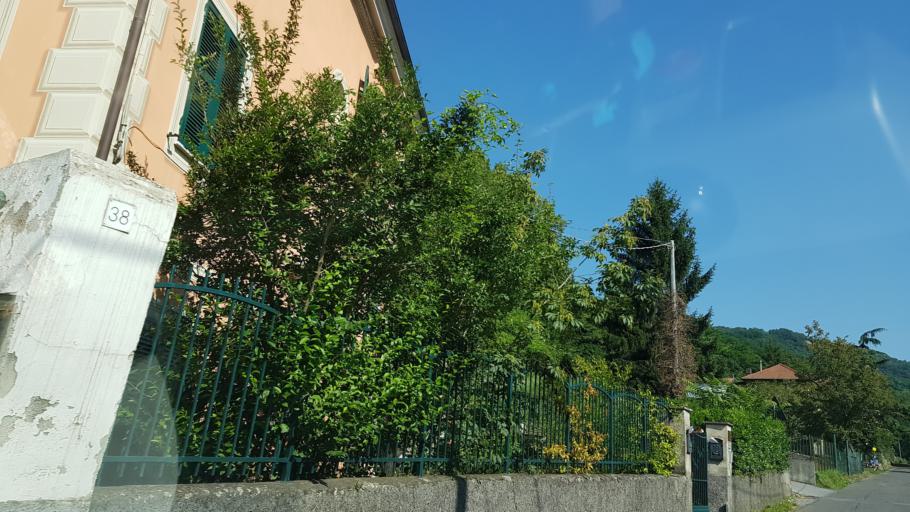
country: IT
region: Liguria
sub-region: Provincia di Genova
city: Serra Ricco
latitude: 44.5126
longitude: 8.9406
